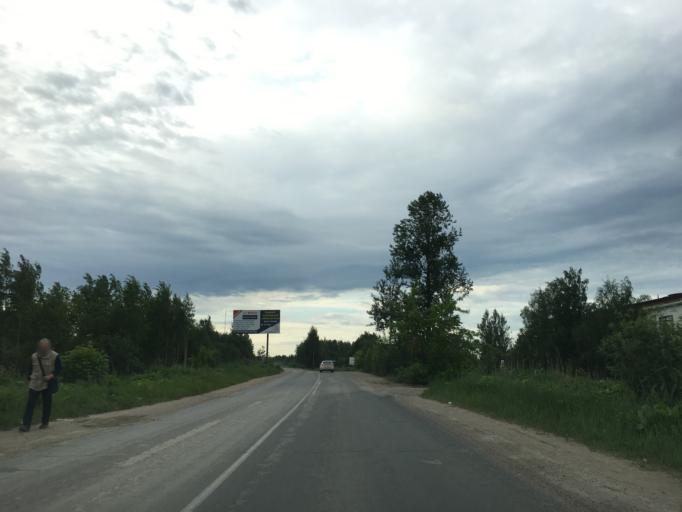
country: RU
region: Pskov
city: Pskov
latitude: 57.8519
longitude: 28.3079
